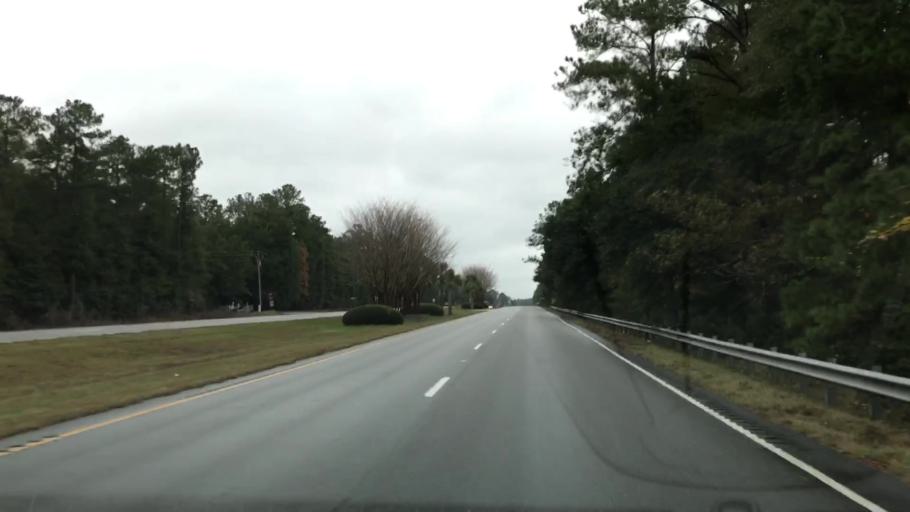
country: US
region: South Carolina
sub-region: Georgetown County
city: Georgetown
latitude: 33.2162
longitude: -79.3802
